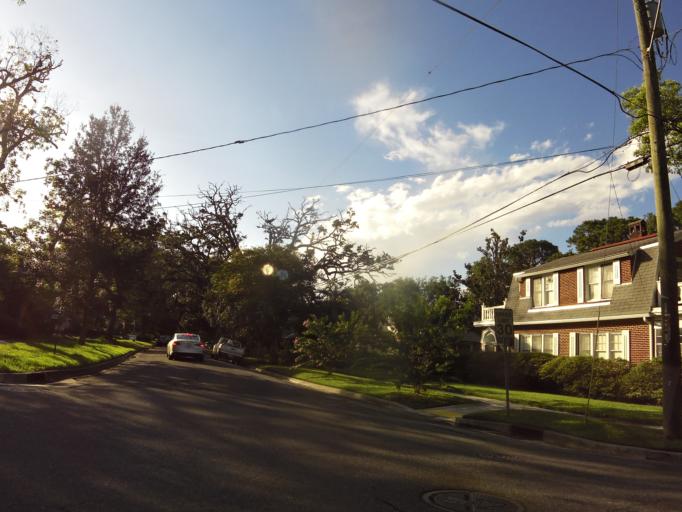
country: US
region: Florida
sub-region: Duval County
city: Jacksonville
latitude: 30.3077
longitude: -81.7076
